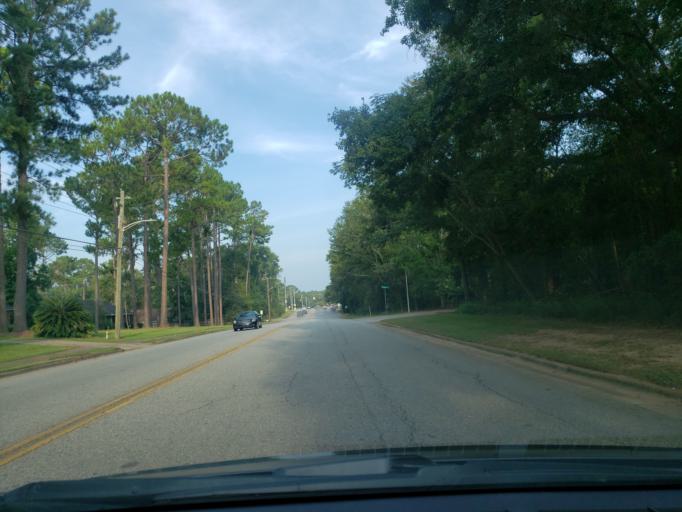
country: US
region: Georgia
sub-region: Dougherty County
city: Albany
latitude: 31.5995
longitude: -84.2167
